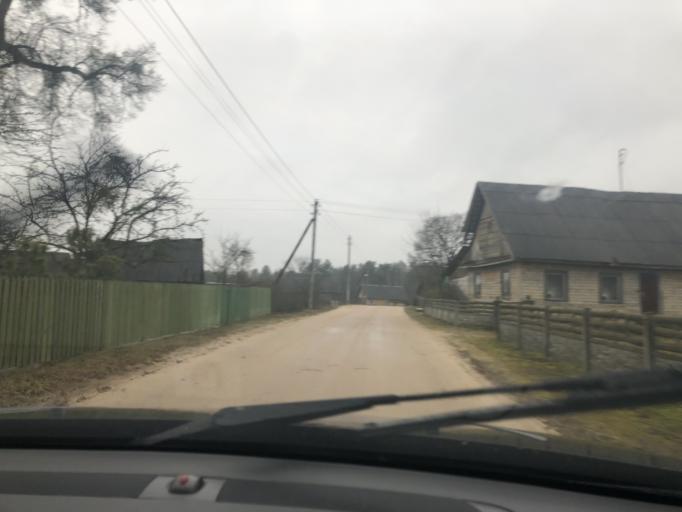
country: BY
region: Grodnenskaya
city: Skidal'
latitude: 53.8597
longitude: 24.2459
